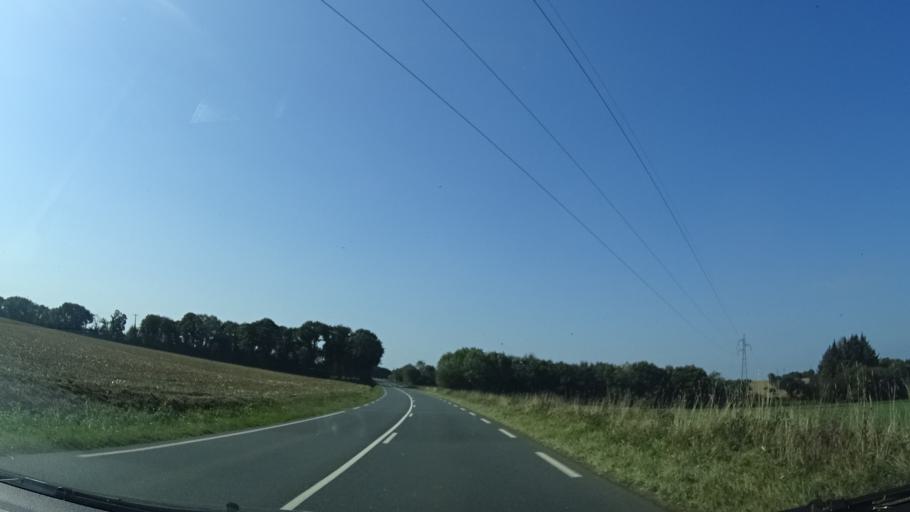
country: FR
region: Brittany
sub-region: Departement du Finistere
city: Cast
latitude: 48.1447
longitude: -4.1584
